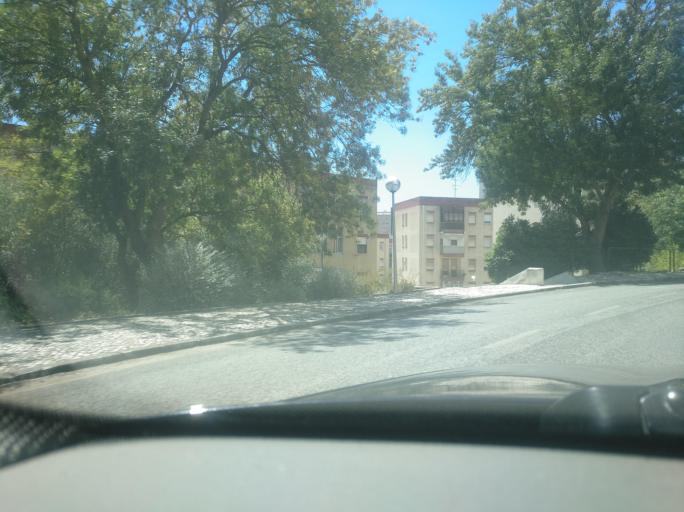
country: PT
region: Lisbon
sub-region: Odivelas
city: Povoa de Santo Adriao
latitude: 38.8116
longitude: -9.1584
